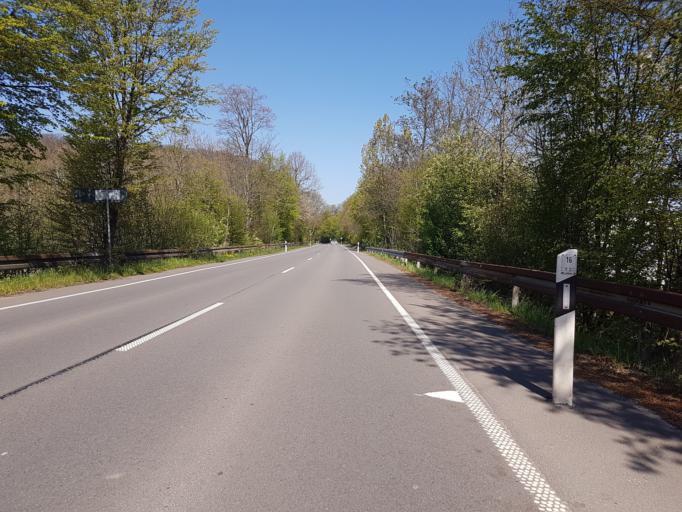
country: DE
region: North Rhine-Westphalia
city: Gevelsberg
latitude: 51.3623
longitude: 7.3292
